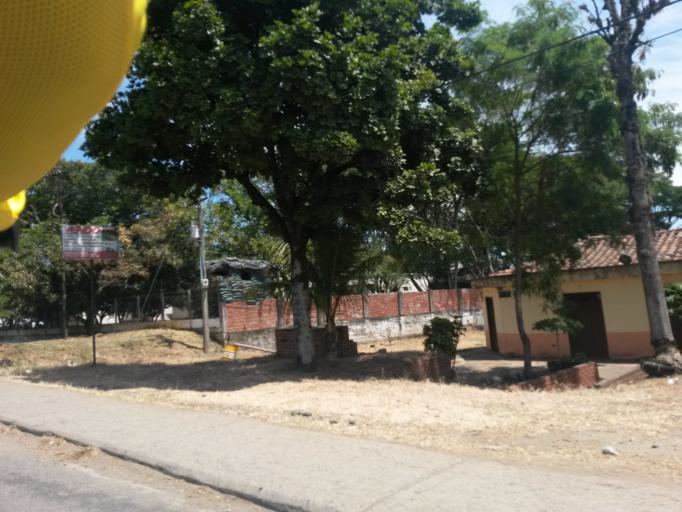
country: CO
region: Cauca
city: Santander de Quilichao
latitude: 3.0146
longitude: -76.4831
